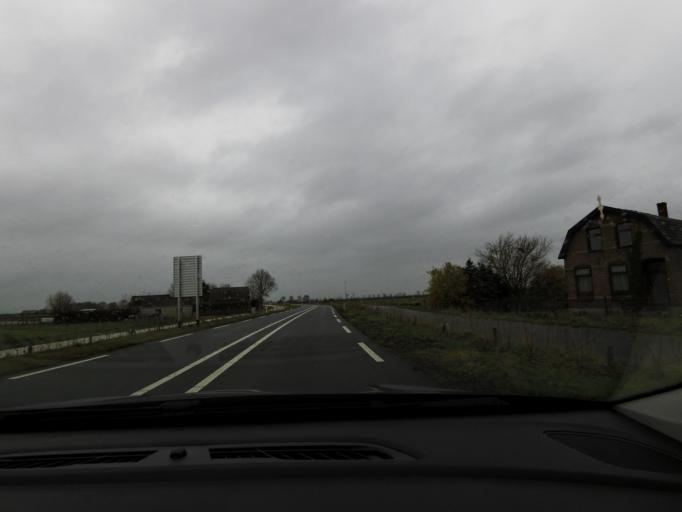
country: NL
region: North Brabant
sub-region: Gemeente Waalwijk
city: Waspik
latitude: 51.7324
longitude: 4.9218
